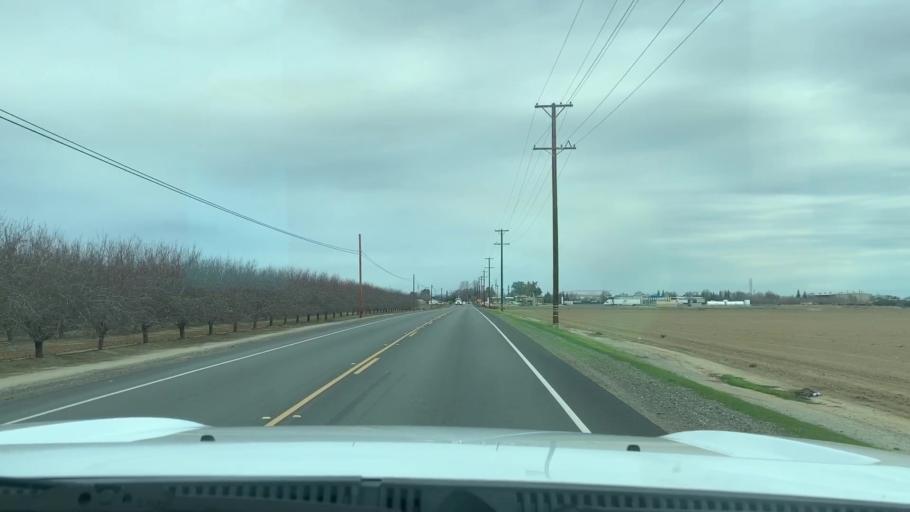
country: US
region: California
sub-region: Kern County
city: Shafter
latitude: 35.4362
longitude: -119.2518
